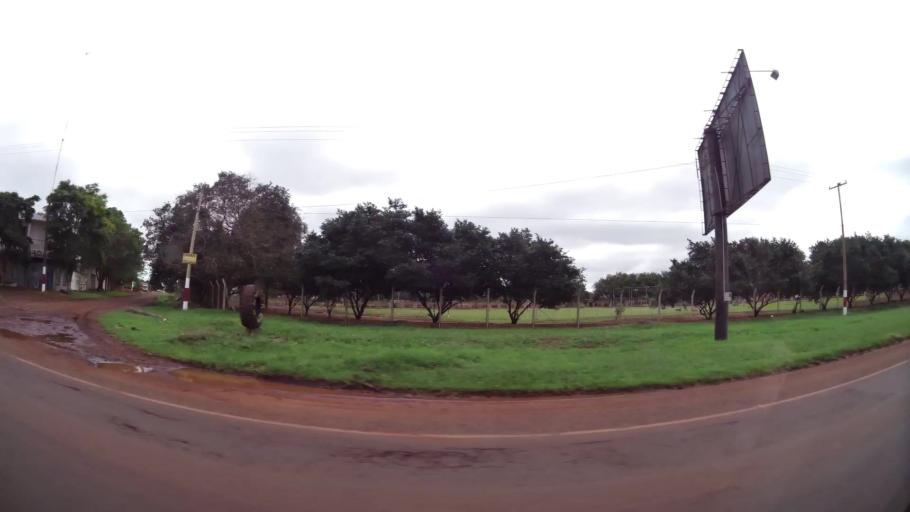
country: PY
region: Alto Parana
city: Ciudad del Este
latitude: -25.3835
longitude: -54.6428
